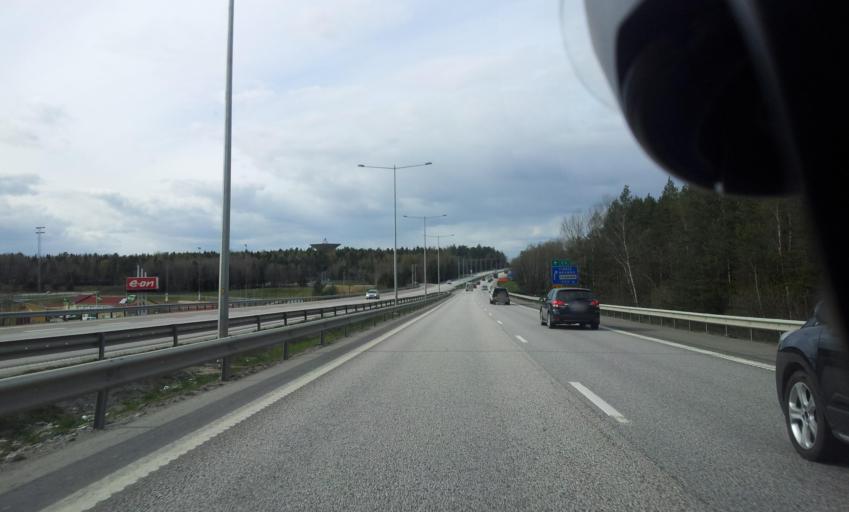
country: SE
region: Stockholm
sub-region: Upplands-Bro Kommun
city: Kungsaengen
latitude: 59.4902
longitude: 17.7519
